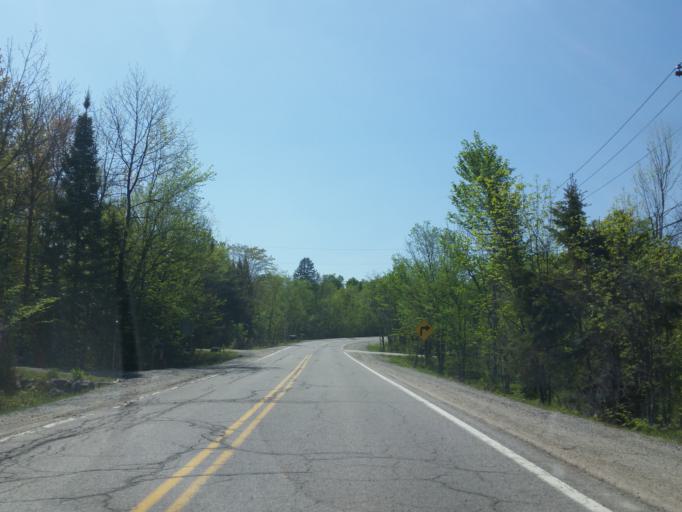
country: CA
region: Quebec
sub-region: Outaouais
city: Wakefield
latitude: 45.5713
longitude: -75.8643
